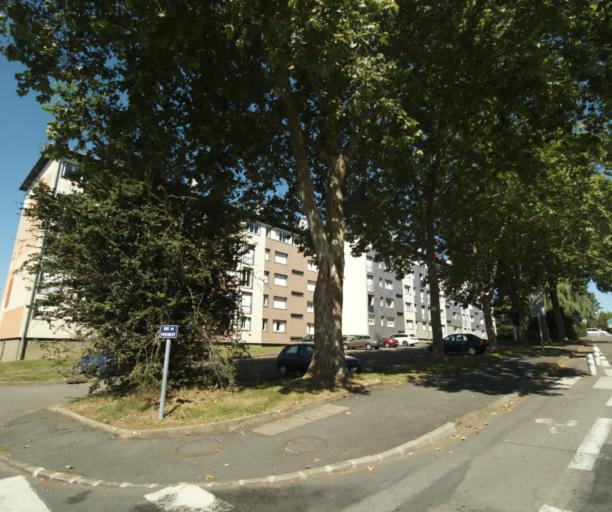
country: FR
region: Pays de la Loire
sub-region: Departement de la Mayenne
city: Laval
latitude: 48.0690
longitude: -0.7491
